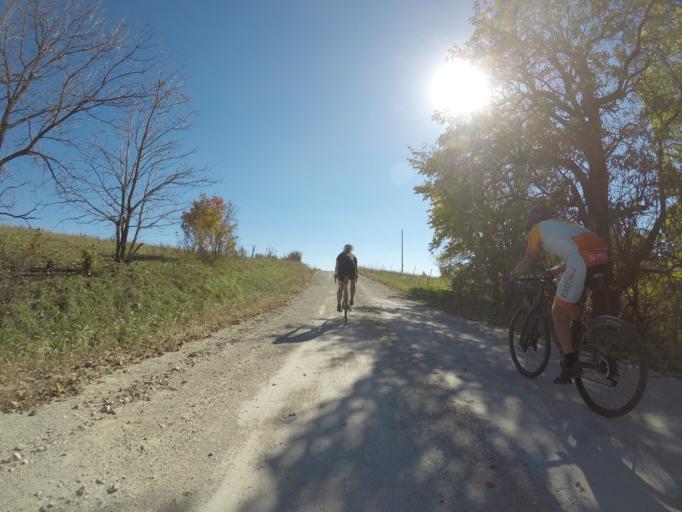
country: US
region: Kansas
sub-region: Wabaunsee County
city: Alma
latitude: 38.9583
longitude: -96.4735
